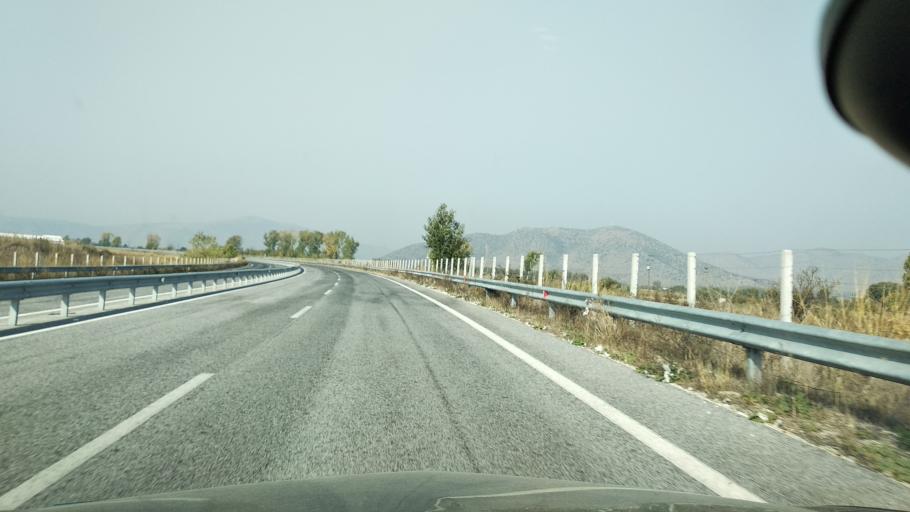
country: GR
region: Thessaly
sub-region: Trikala
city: Farkadona
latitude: 39.5849
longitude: 22.0453
